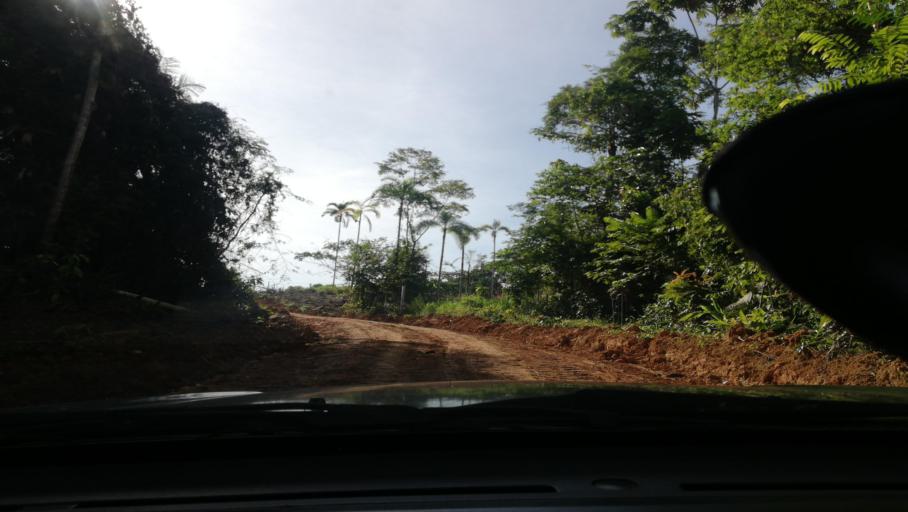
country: PE
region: Loreto
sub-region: Provincia de Loreto
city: Nauta
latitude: -4.3376
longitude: -73.5121
